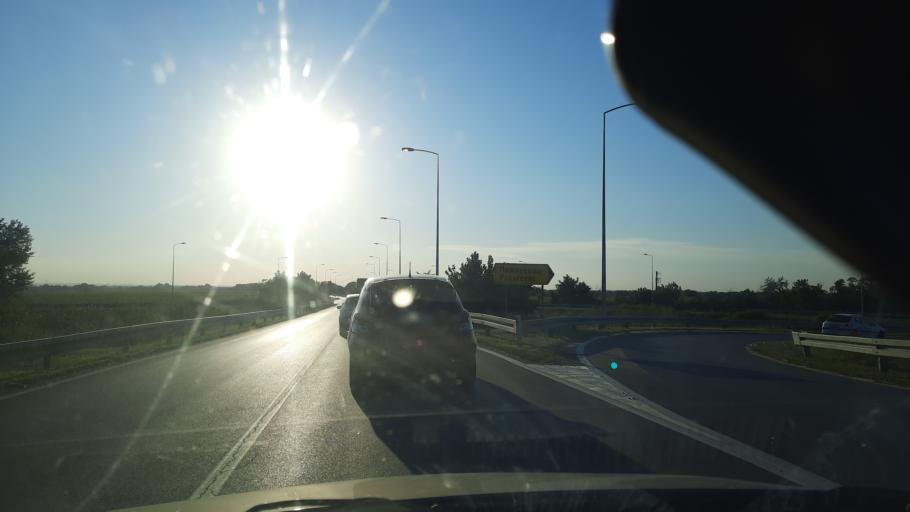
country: RS
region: Central Serbia
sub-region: Branicevski Okrug
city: Pozarevac
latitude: 44.5994
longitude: 21.1490
